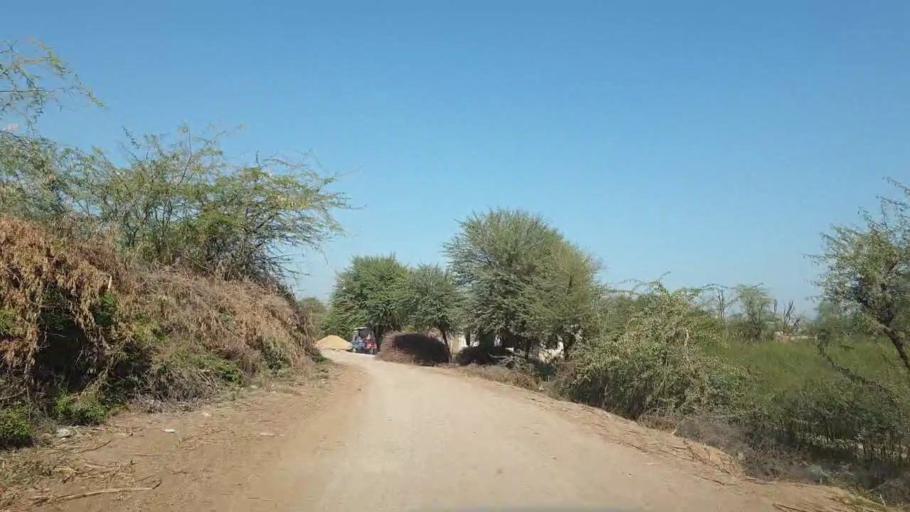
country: PK
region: Sindh
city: Tando Adam
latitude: 25.6558
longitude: 68.6820
